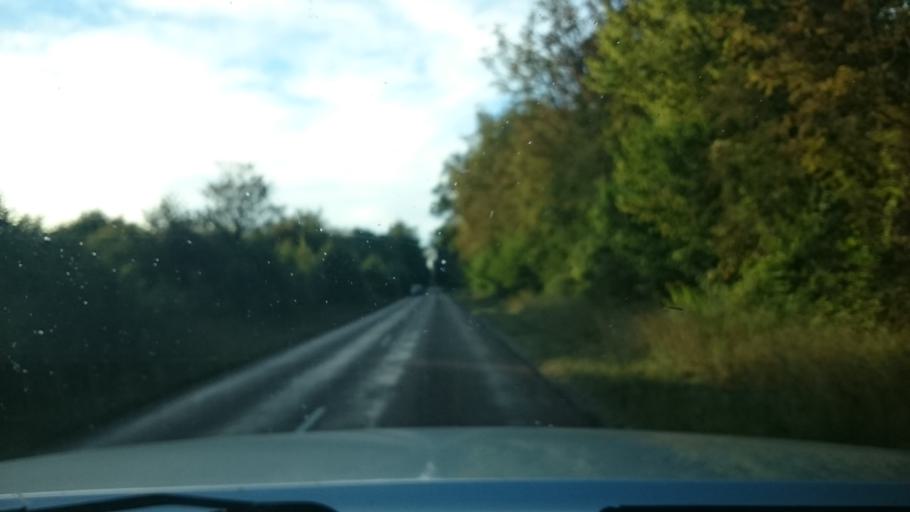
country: FR
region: Ile-de-France
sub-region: Departement de Seine-et-Marne
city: Samoreau
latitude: 48.4002
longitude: 2.7598
